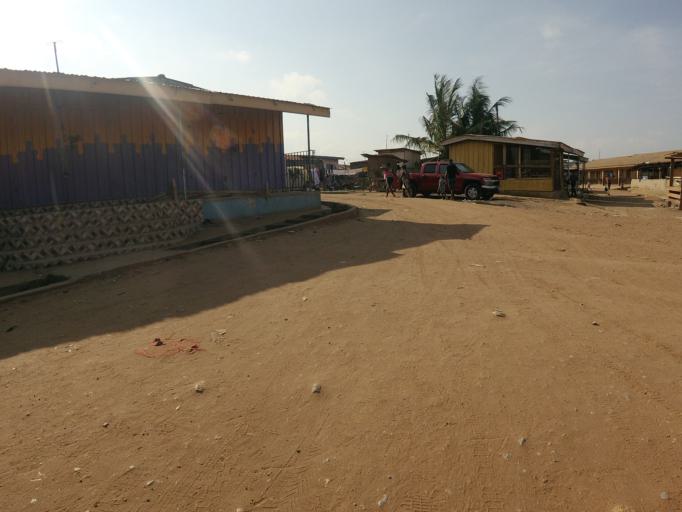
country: GH
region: Greater Accra
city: Dome
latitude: 5.6564
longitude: -0.2672
